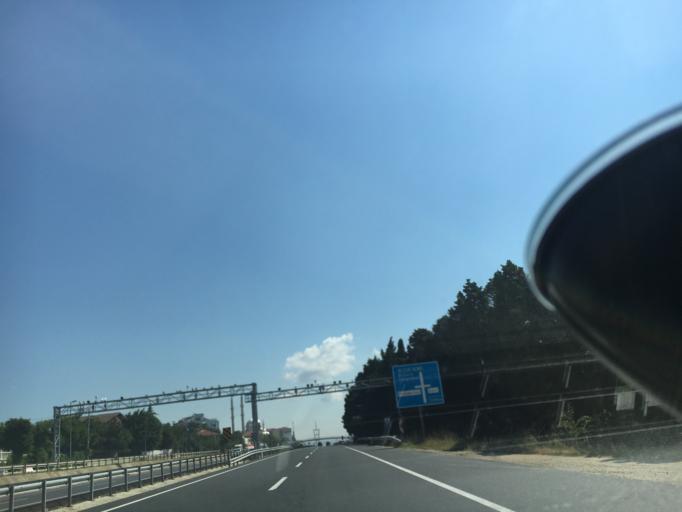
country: TR
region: Tekirdag
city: Sultankoy
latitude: 41.0442
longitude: 28.0368
